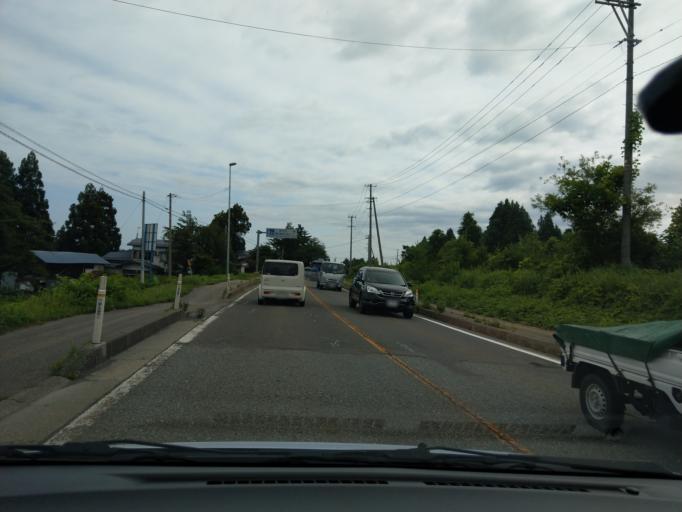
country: JP
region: Akita
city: Yokotemachi
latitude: 39.3554
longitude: 140.5623
